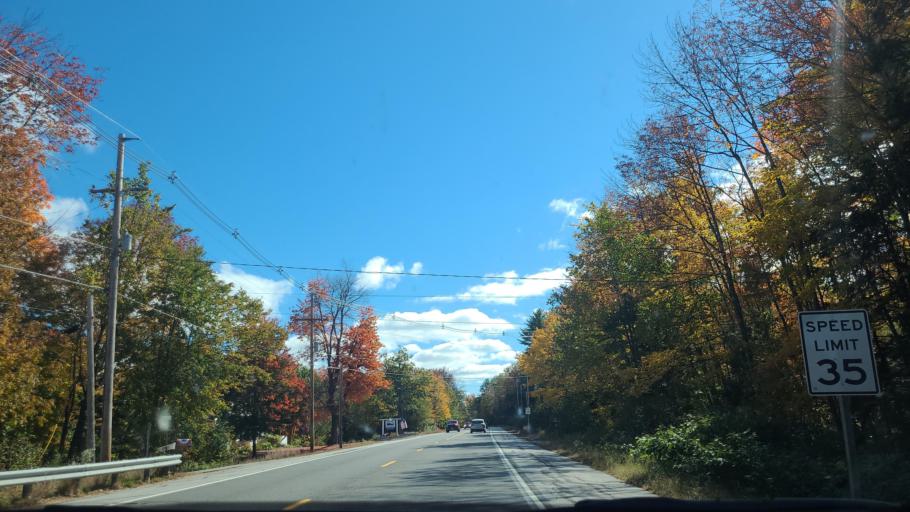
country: US
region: Maine
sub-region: Cumberland County
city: Bridgton
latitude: 43.9766
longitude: -70.6201
